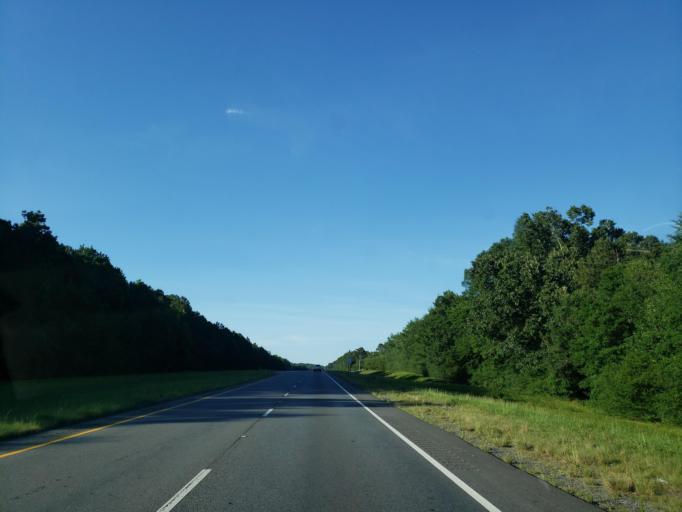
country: US
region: Georgia
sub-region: Floyd County
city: Shannon
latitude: 34.3180
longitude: -85.1059
